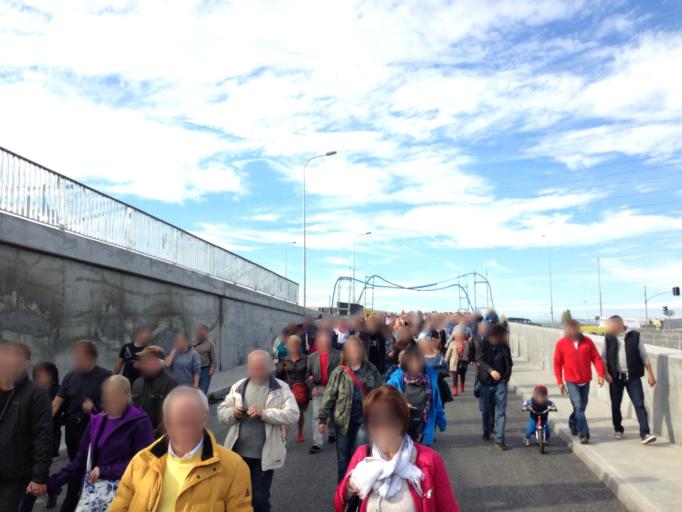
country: PL
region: Pomeranian Voivodeship
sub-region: Gdansk
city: Gdansk
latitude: 54.3872
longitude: 18.6520
